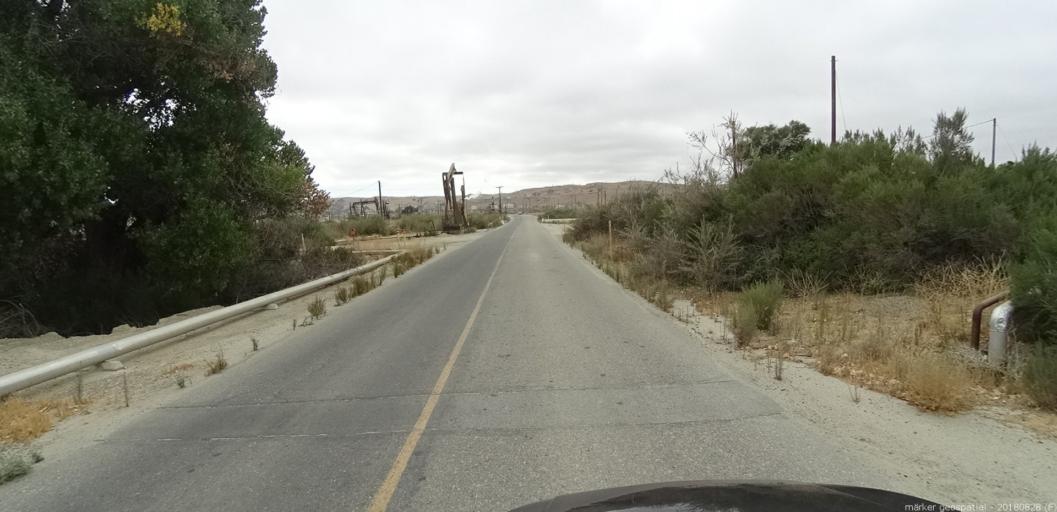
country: US
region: California
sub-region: San Luis Obispo County
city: Lake Nacimiento
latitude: 35.9559
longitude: -120.8755
